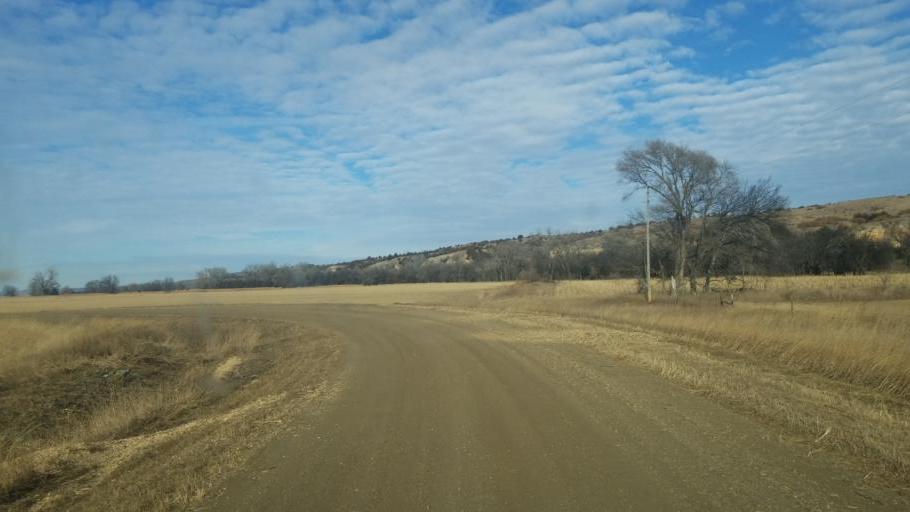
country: US
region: South Dakota
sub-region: Charles Mix County
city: Wagner
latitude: 42.9509
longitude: -98.4463
